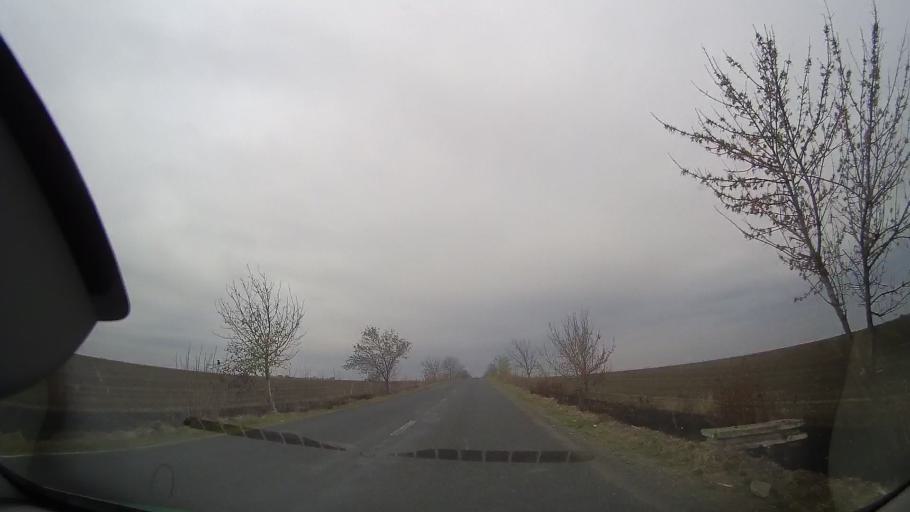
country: RO
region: Buzau
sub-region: Comuna Padina
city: Padina
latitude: 44.7812
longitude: 27.1518
